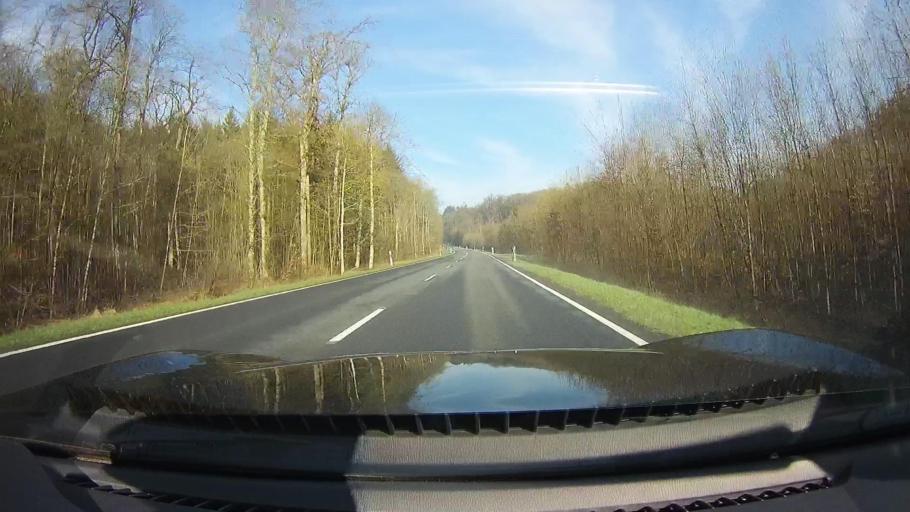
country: DE
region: Baden-Wuerttemberg
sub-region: Karlsruhe Region
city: Seckach
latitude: 49.4179
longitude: 9.3142
